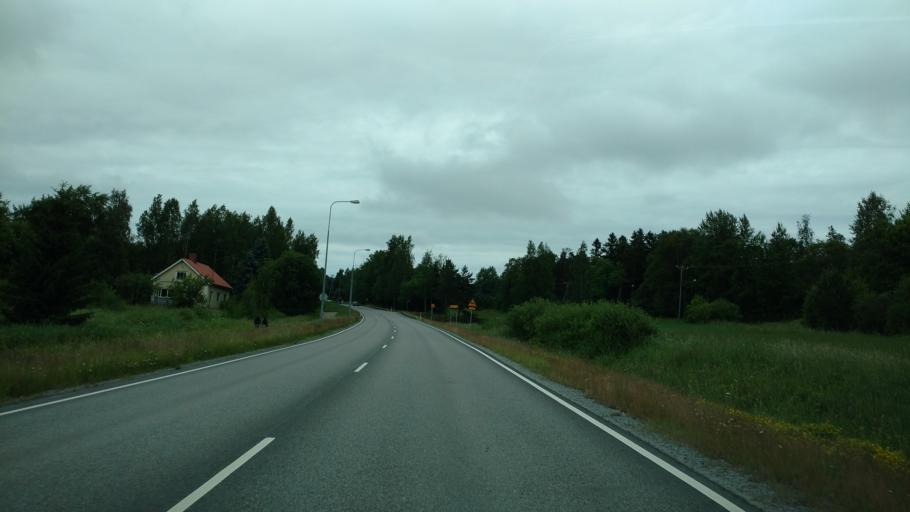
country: FI
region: Varsinais-Suomi
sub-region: Salo
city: Halikko
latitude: 60.4331
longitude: 23.0478
